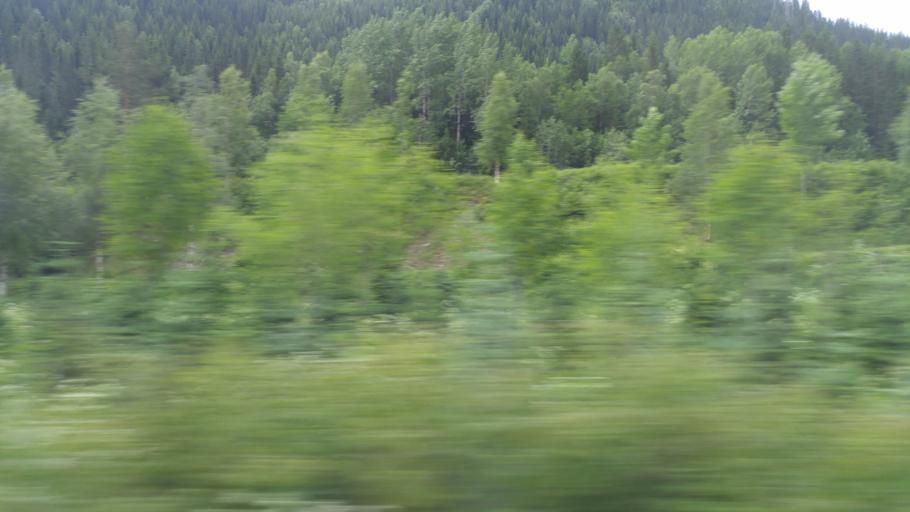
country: NO
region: Nord-Trondelag
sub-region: Levanger
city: Levanger
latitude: 63.4570
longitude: 11.4226
